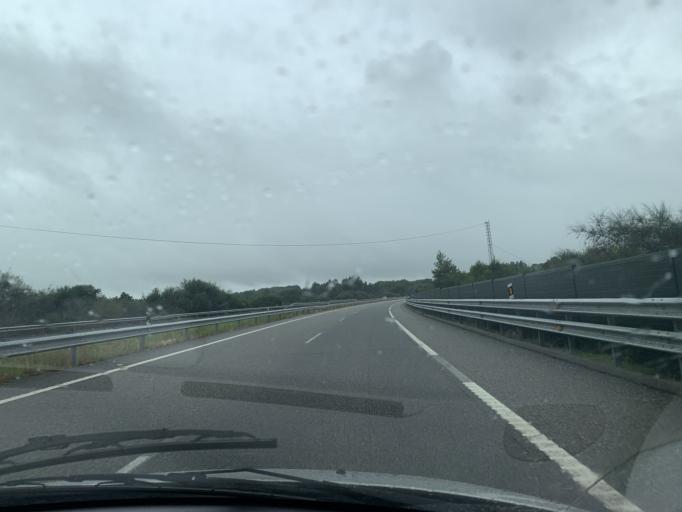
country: ES
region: Galicia
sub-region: Provincia de Lugo
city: Vilalba
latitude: 43.3296
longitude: -7.5872
